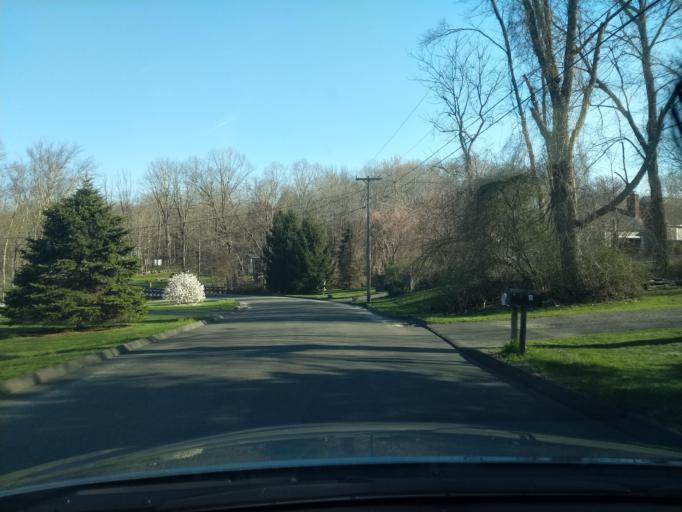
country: US
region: Connecticut
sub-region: Fairfield County
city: Newtown
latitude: 41.3780
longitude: -73.2924
